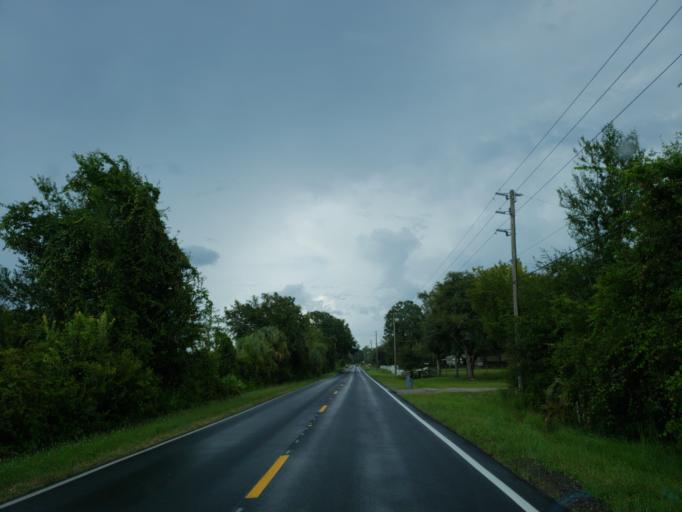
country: US
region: Florida
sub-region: Pasco County
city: Land O' Lakes
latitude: 28.2889
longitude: -82.4340
